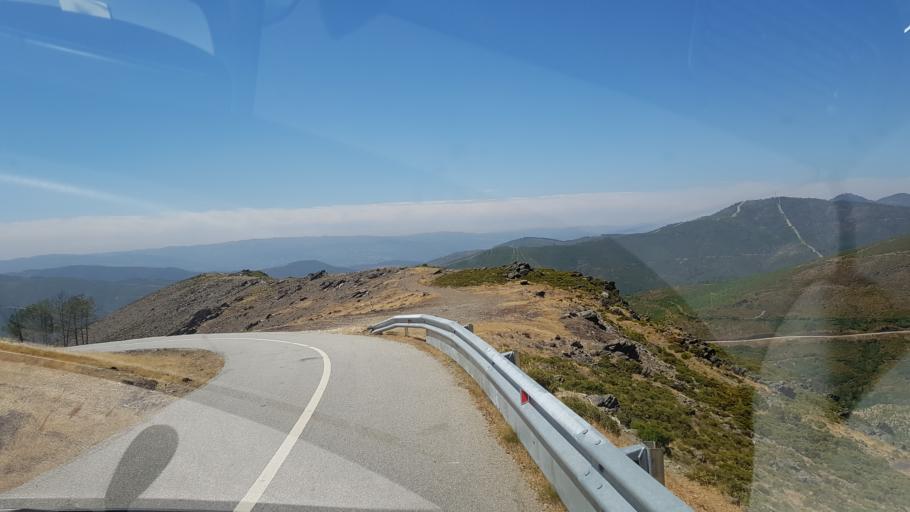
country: PT
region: Vila Real
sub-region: Mondim de Basto
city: Mondim de Basto
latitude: 41.3409
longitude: -7.8791
